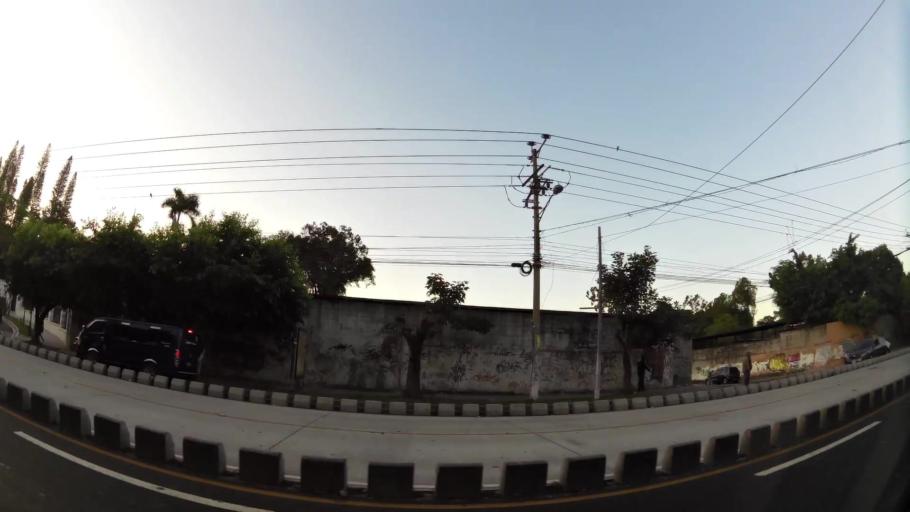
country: SV
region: San Salvador
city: San Salvador
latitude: 13.7034
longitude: -89.1982
